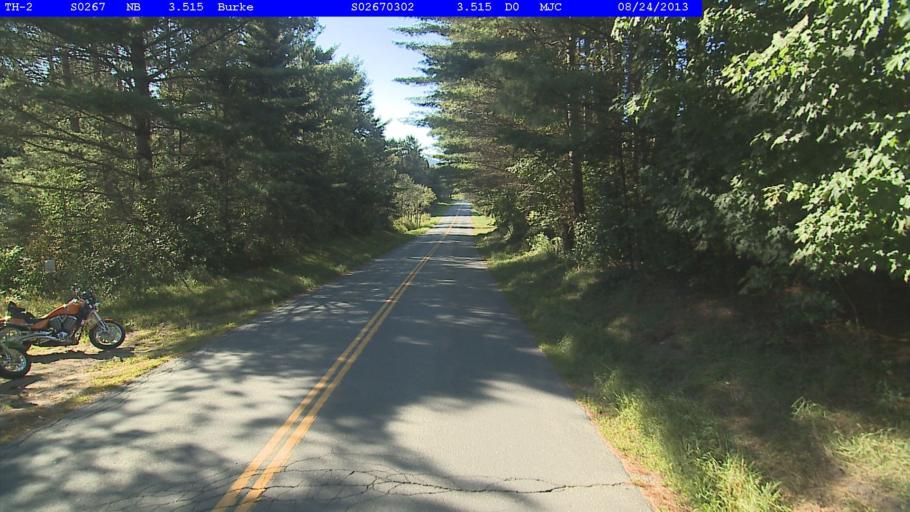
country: US
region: Vermont
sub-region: Caledonia County
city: Lyndonville
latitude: 44.6267
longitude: -71.9625
